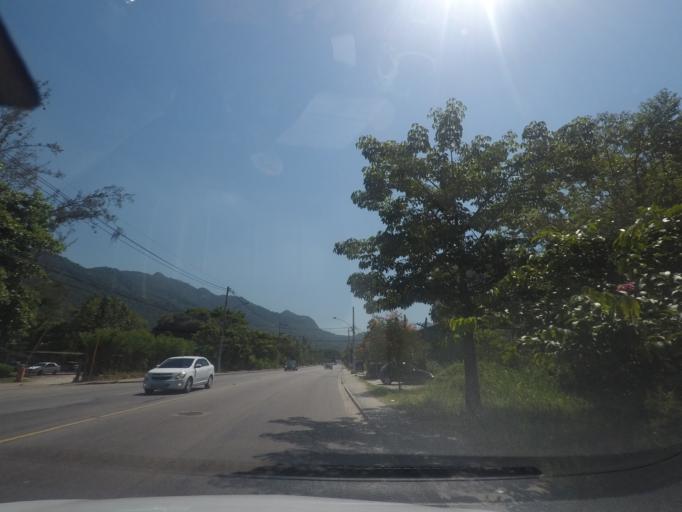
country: BR
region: Rio de Janeiro
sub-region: Nilopolis
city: Nilopolis
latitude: -22.9843
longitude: -43.4720
